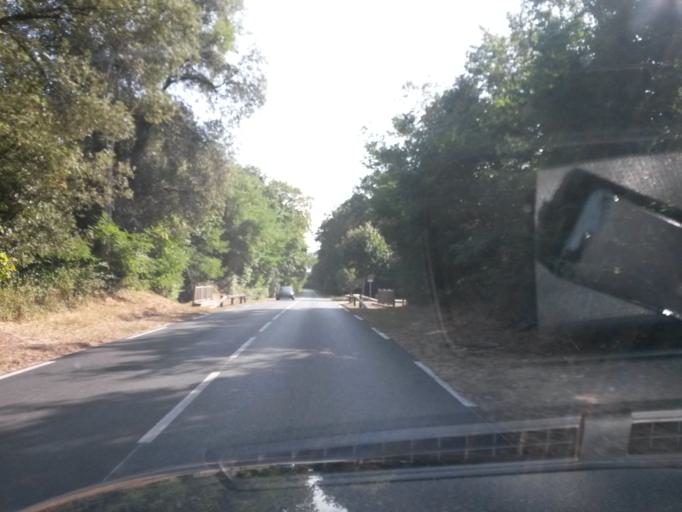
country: FR
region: Pays de la Loire
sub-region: Departement de la Vendee
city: Olonne-sur-Mer
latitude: 46.5766
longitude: -1.8230
